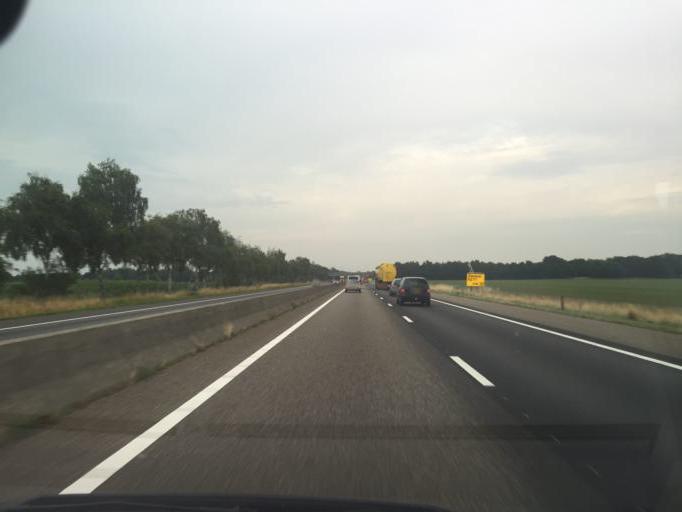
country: NL
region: Limburg
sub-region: Gemeente Peel en Maas
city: Maasbree
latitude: 51.3779
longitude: 5.9523
